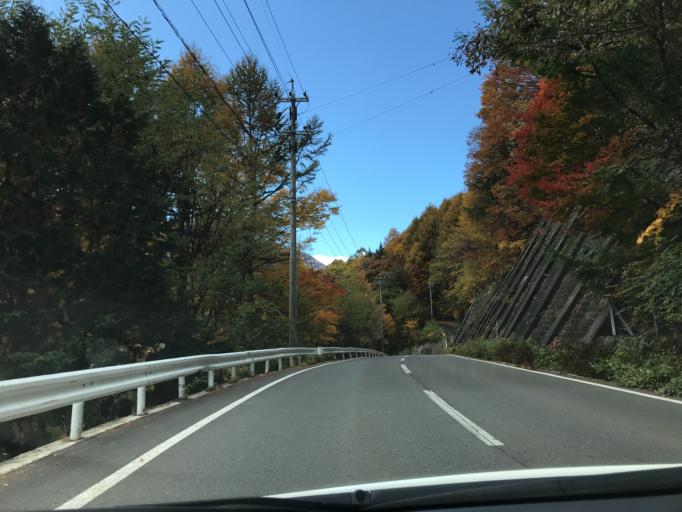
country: JP
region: Nagano
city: Toyoshina
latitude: 36.1326
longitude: 137.6712
